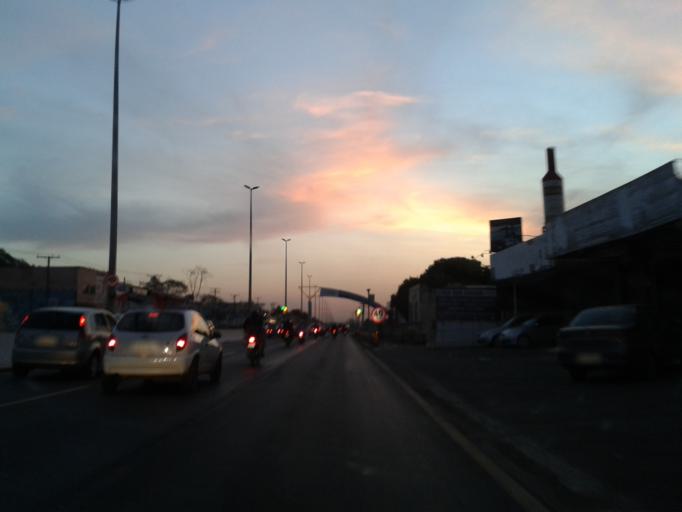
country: BR
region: Goias
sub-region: Goiania
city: Goiania
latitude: -16.6599
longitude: -49.3411
